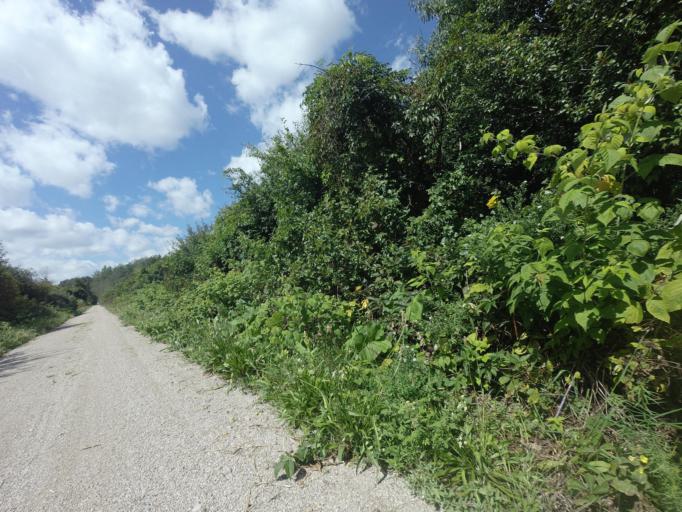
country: CA
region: Ontario
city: Huron East
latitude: 43.6327
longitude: -81.1843
